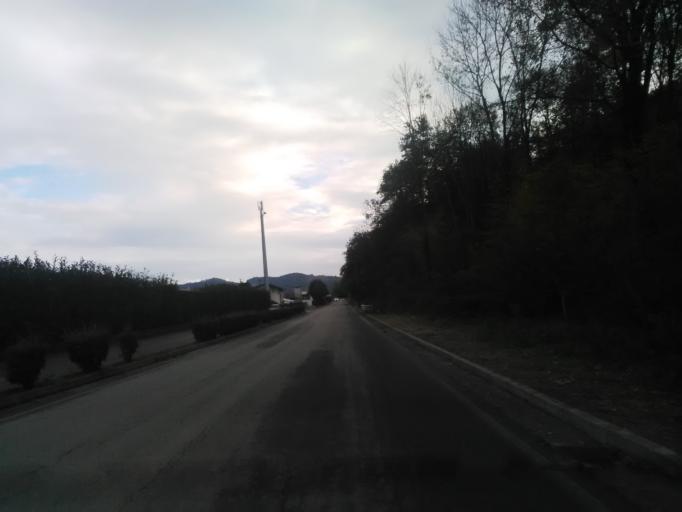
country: IT
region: Piedmont
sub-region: Provincia di Novara
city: Pella
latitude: 45.7830
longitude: 8.3826
